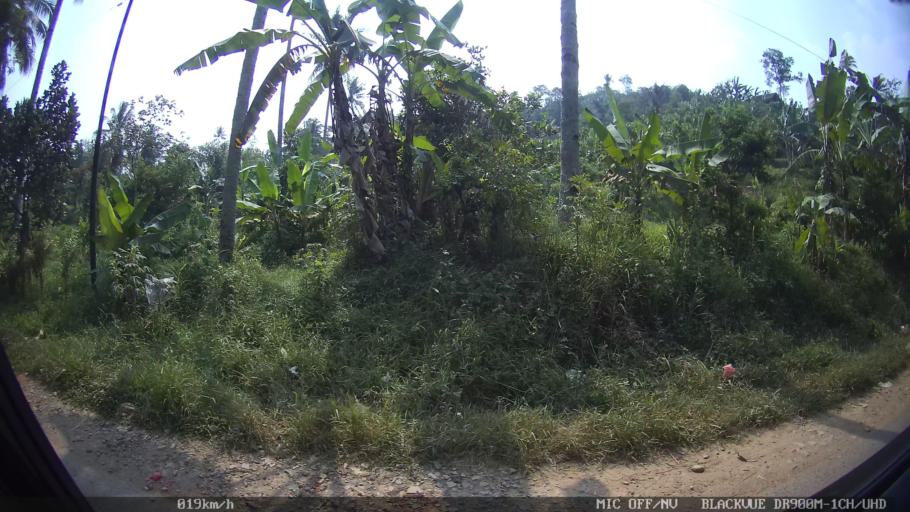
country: ID
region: Lampung
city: Pringsewu
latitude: -5.3892
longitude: 104.9941
